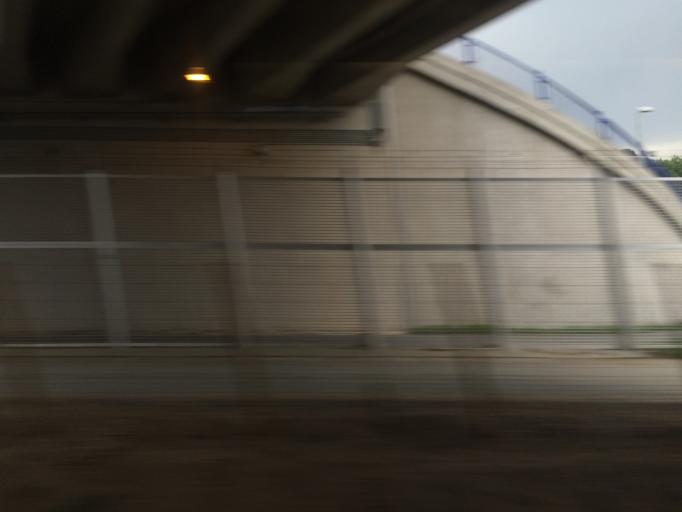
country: DE
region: Hesse
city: Kelsterbach
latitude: 50.0363
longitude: 8.5167
